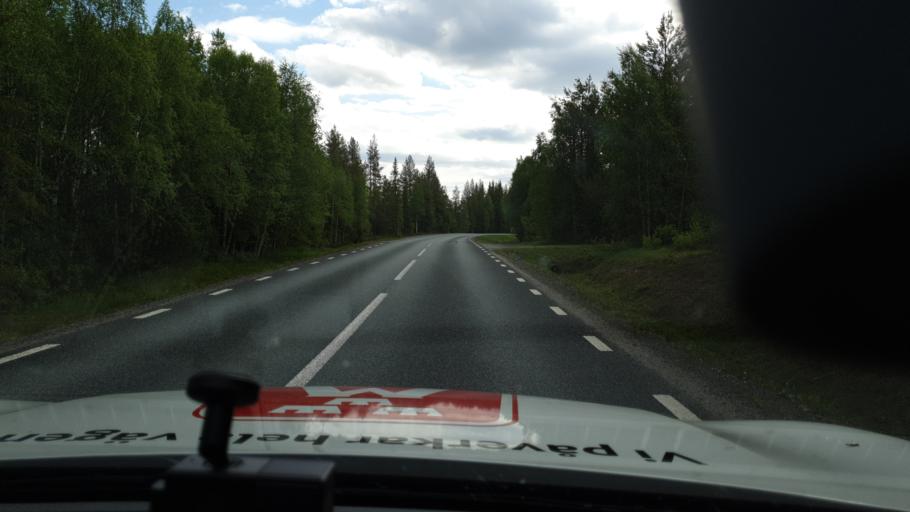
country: SE
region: Vaesterbotten
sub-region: Sorsele Kommun
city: Sorsele
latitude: 65.3850
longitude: 17.5775
